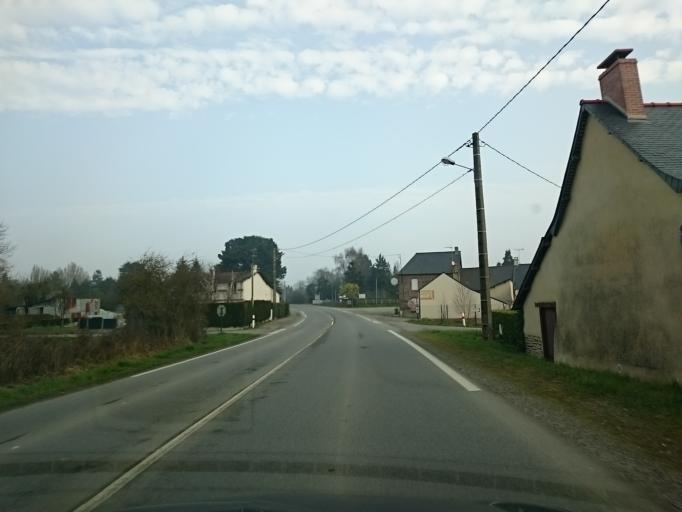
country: FR
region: Brittany
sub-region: Departement d'Ille-et-Vilaine
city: Chatillon-sur-Seiche
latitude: 48.0626
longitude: -1.6636
